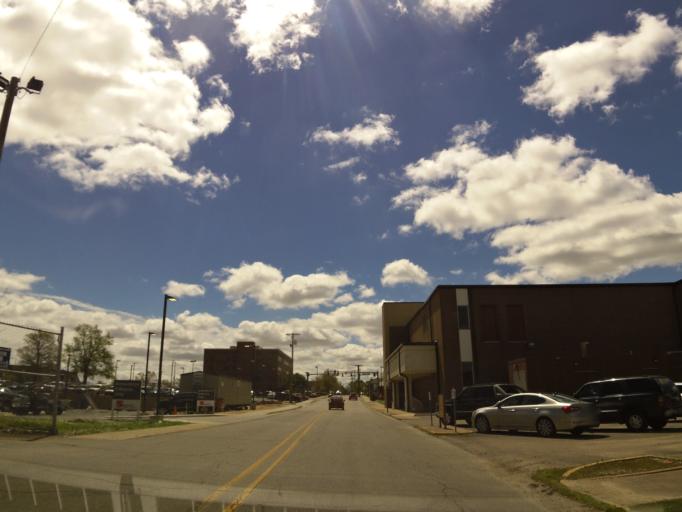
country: US
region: Arkansas
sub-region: Craighead County
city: Jonesboro
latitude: 35.8369
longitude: -90.7041
